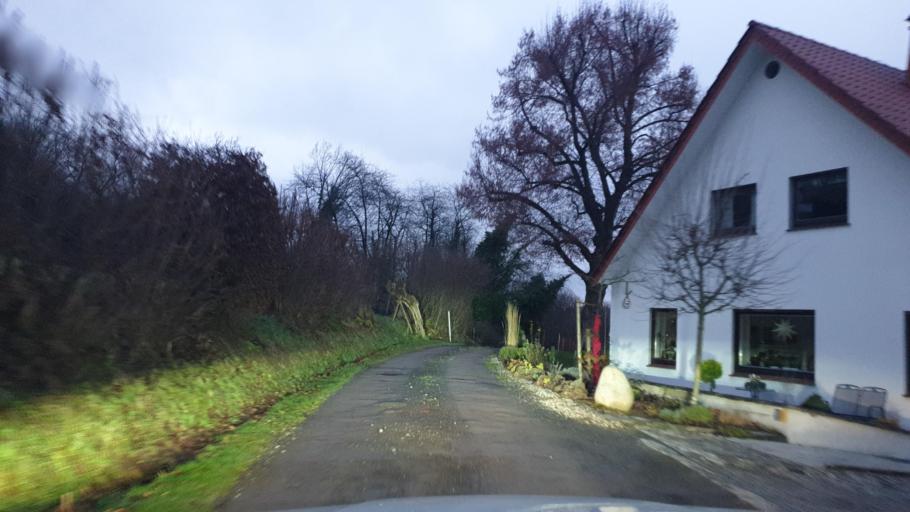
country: DE
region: North Rhine-Westphalia
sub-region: Regierungsbezirk Detmold
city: Vlotho
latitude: 52.1627
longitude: 8.8739
